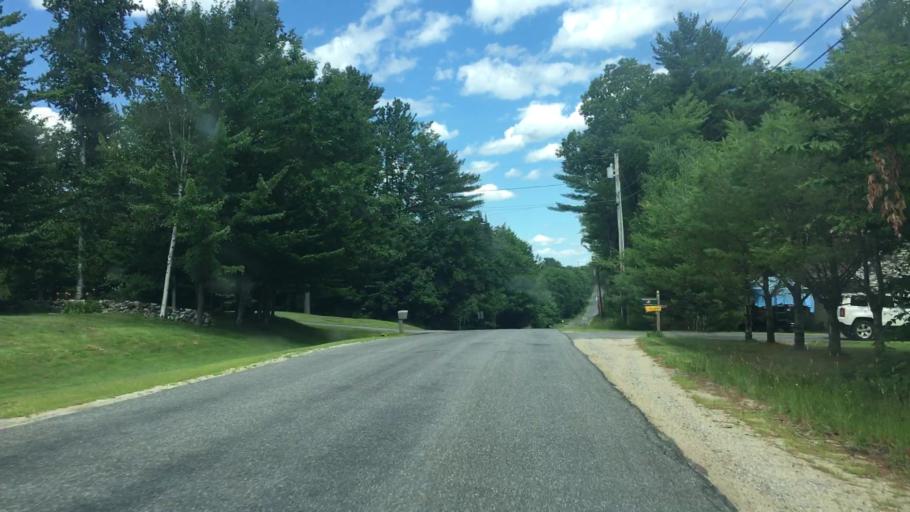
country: US
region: Maine
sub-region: Franklin County
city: Jay
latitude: 44.5352
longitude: -70.2067
